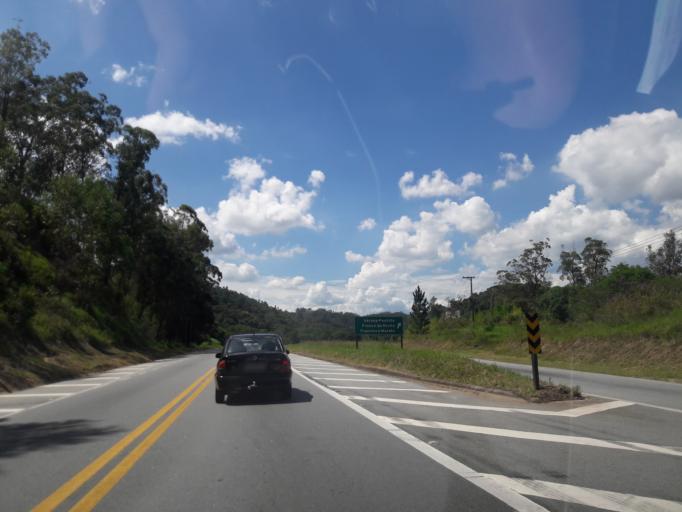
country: BR
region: Sao Paulo
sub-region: Francisco Morato
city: Francisco Morato
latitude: -23.2878
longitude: -46.8003
